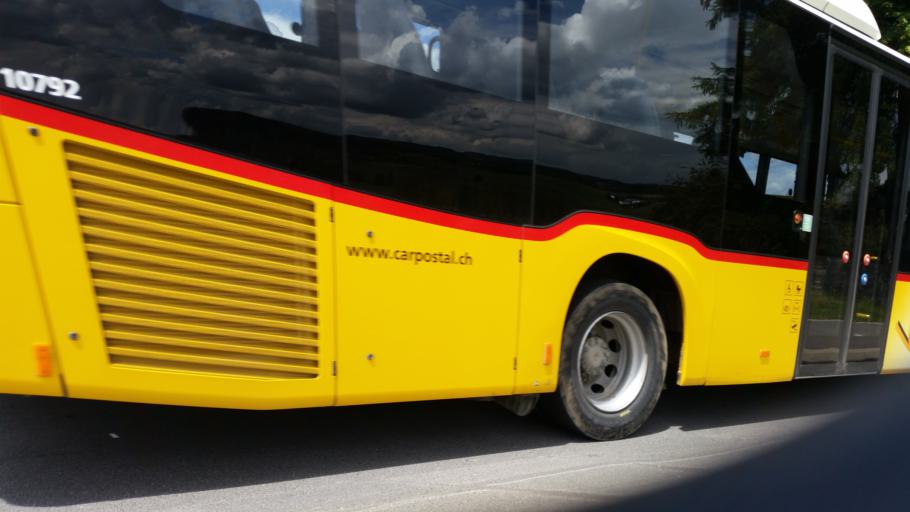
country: CH
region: Vaud
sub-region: Lausanne District
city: Cheseaux
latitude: 46.6192
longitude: 6.5964
